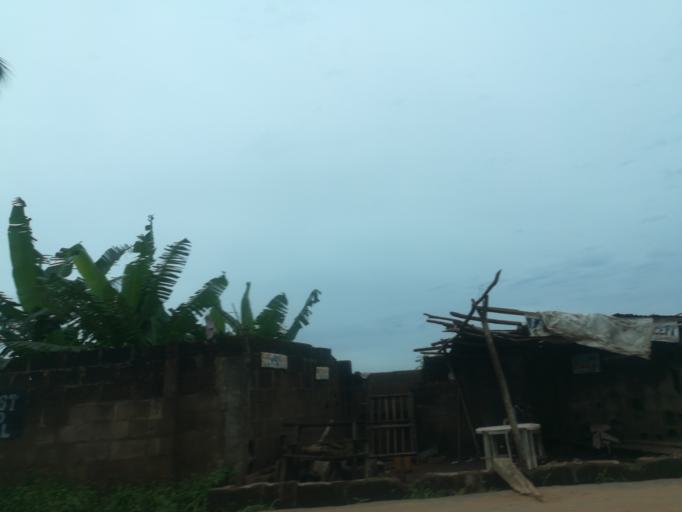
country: NG
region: Oyo
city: Ibadan
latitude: 7.3936
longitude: 3.9748
